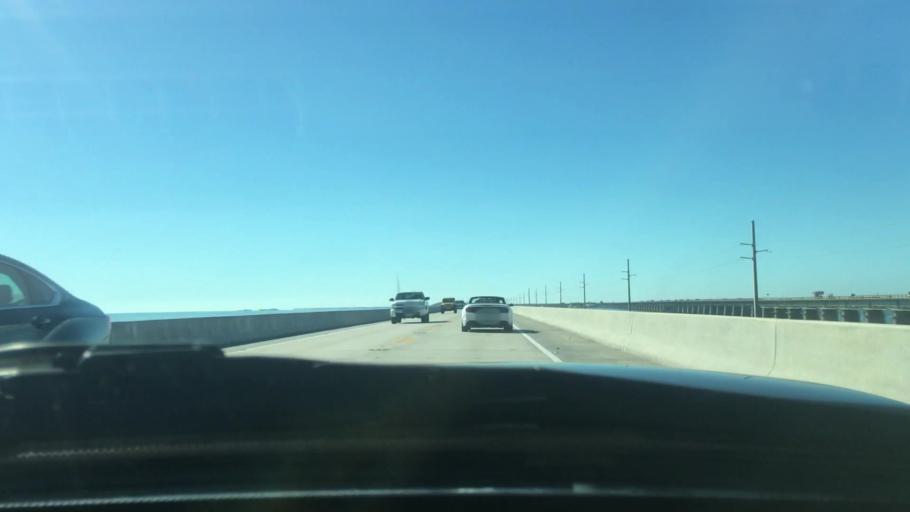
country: US
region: Florida
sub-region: Monroe County
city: Marathon
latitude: 24.7048
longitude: -81.1376
